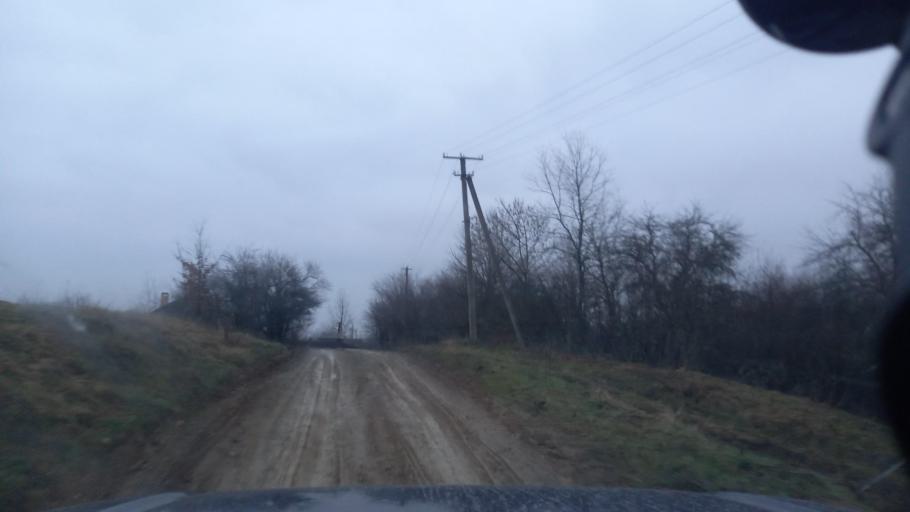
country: RU
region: Krasnodarskiy
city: Saratovskaya
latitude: 44.6463
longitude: 39.3162
